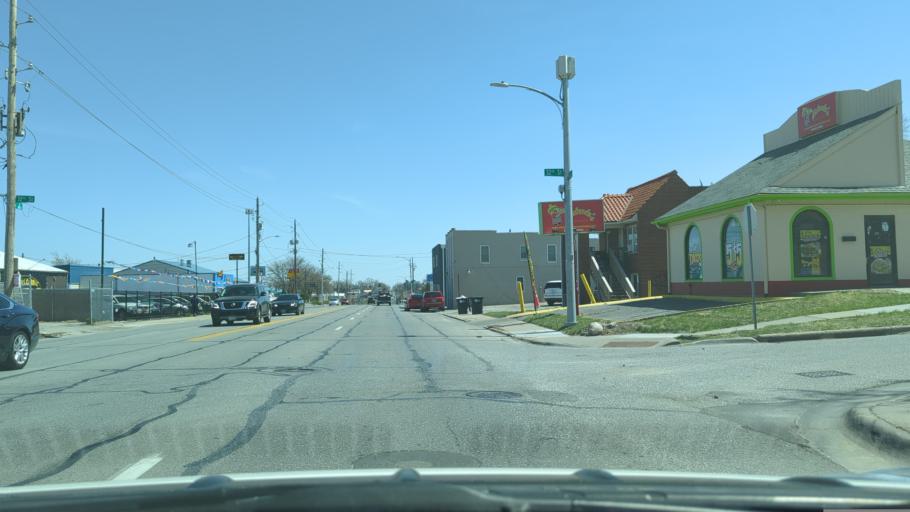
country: US
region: Nebraska
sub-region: Douglas County
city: Omaha
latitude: 41.2054
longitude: -95.9614
